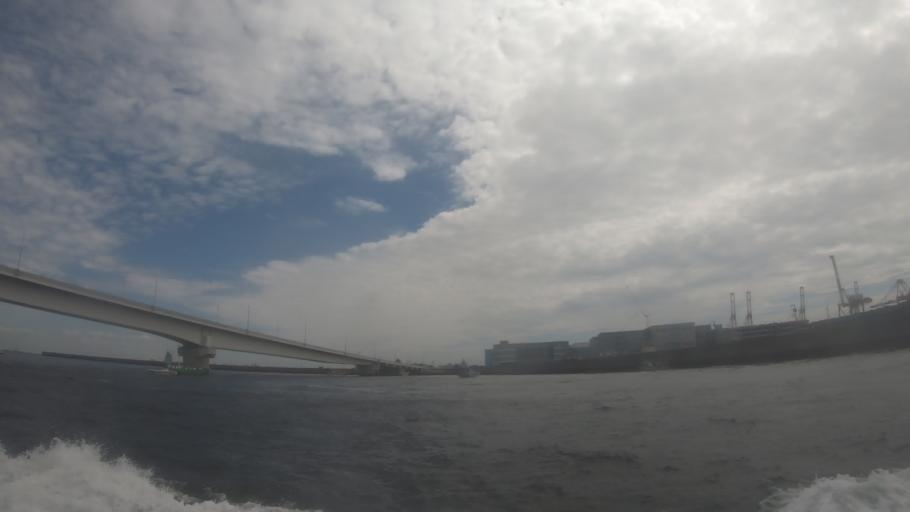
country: JP
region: Kanagawa
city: Yokohama
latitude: 35.4109
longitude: 139.6803
